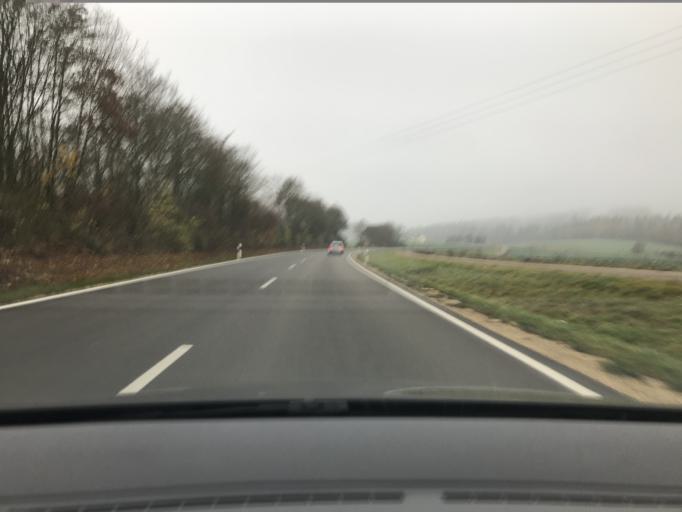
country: DE
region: Bavaria
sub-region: Swabia
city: Fremdingen
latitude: 48.9839
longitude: 10.4362
